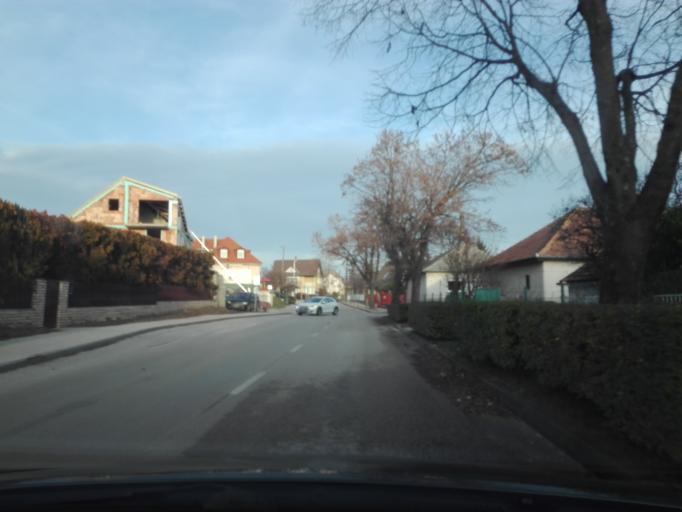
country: HU
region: Veszprem
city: Balatonfured
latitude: 46.9594
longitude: 17.8791
